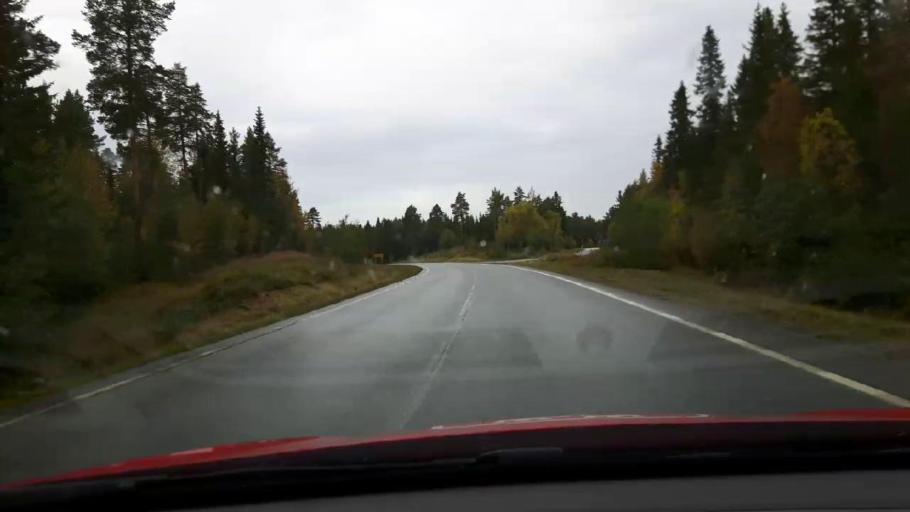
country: SE
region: Jaemtland
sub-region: Bergs Kommun
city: Hoverberg
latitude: 62.9020
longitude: 14.3427
